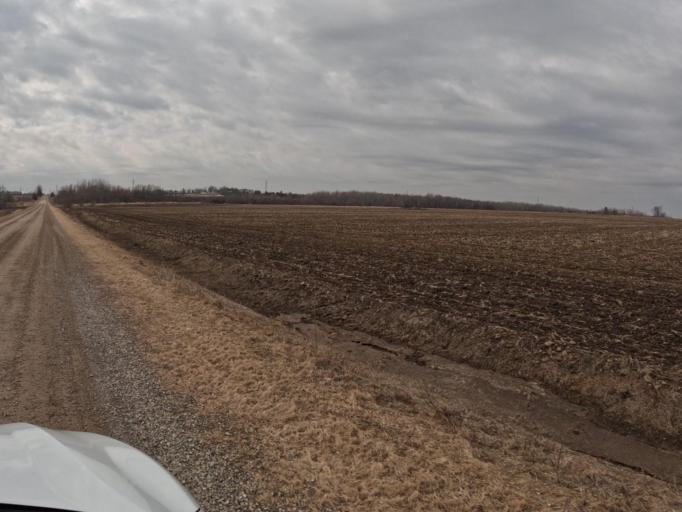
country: CA
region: Ontario
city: Orangeville
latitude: 43.9380
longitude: -80.1897
